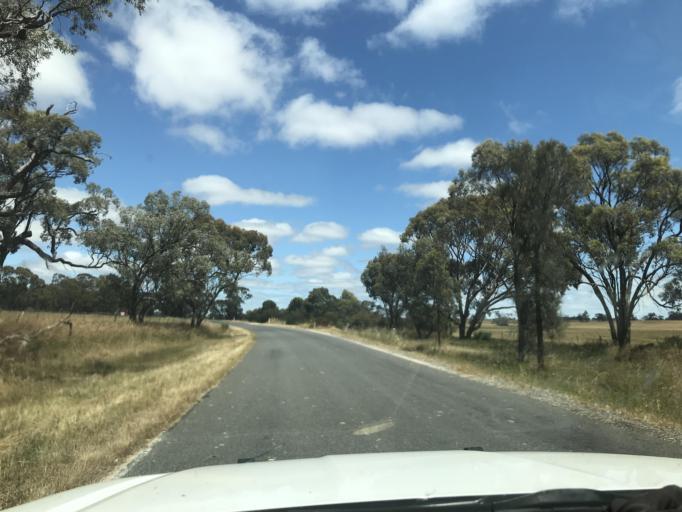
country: AU
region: South Australia
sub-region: Tatiara
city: Bordertown
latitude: -36.3108
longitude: 141.0236
